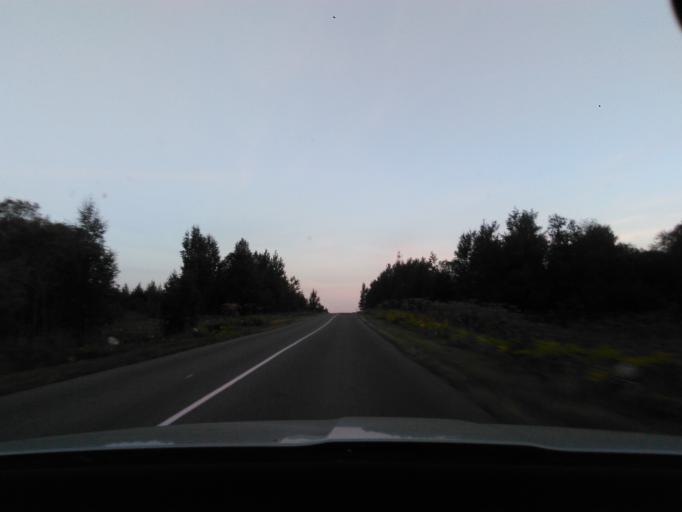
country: RU
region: Moskovskaya
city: Klin
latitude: 56.2373
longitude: 36.7522
